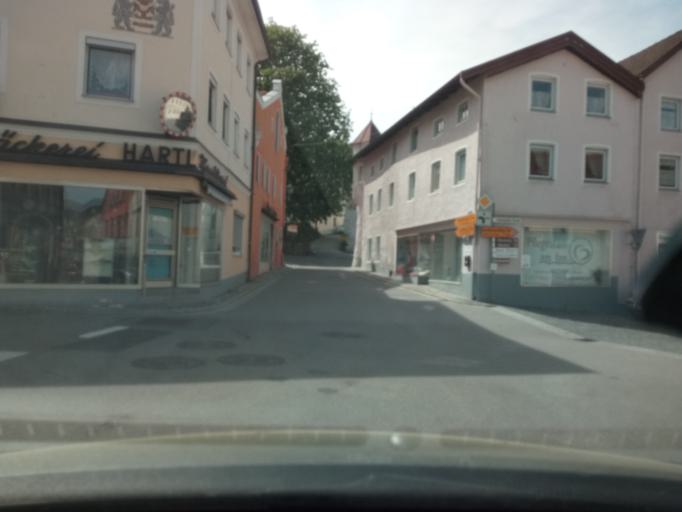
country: DE
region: Bavaria
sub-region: Upper Bavaria
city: Kraiburg am Inn
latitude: 48.1834
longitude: 12.4278
